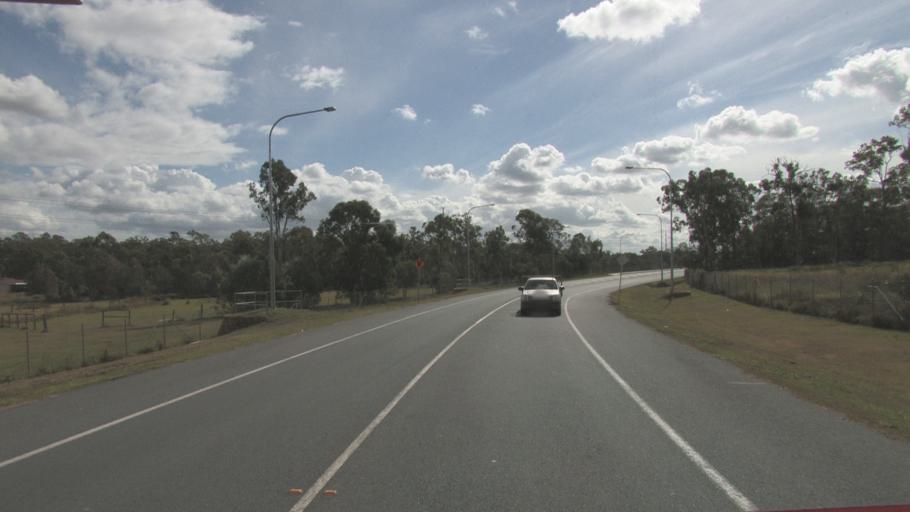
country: AU
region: Queensland
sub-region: Logan
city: Logan Reserve
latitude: -27.6908
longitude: 153.0696
